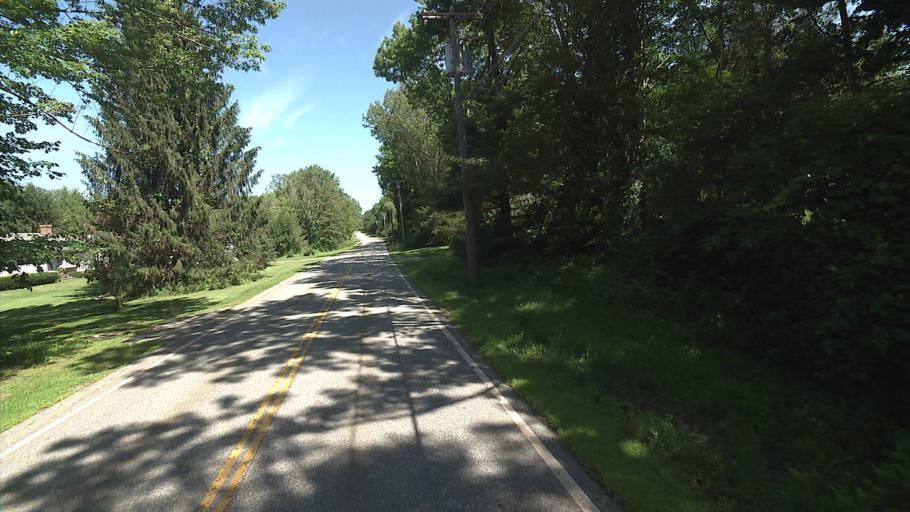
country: US
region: Connecticut
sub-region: Windham County
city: Windham
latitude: 41.7086
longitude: -72.0674
